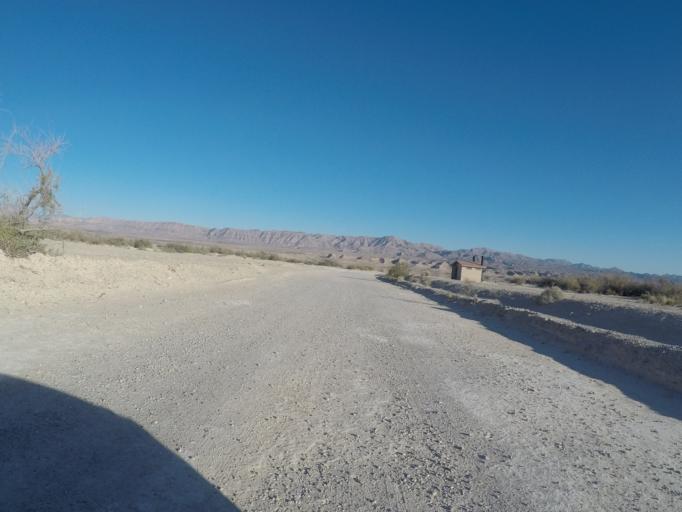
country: US
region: Nevada
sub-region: Clark County
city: Moapa Valley
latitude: 36.3786
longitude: -114.3994
